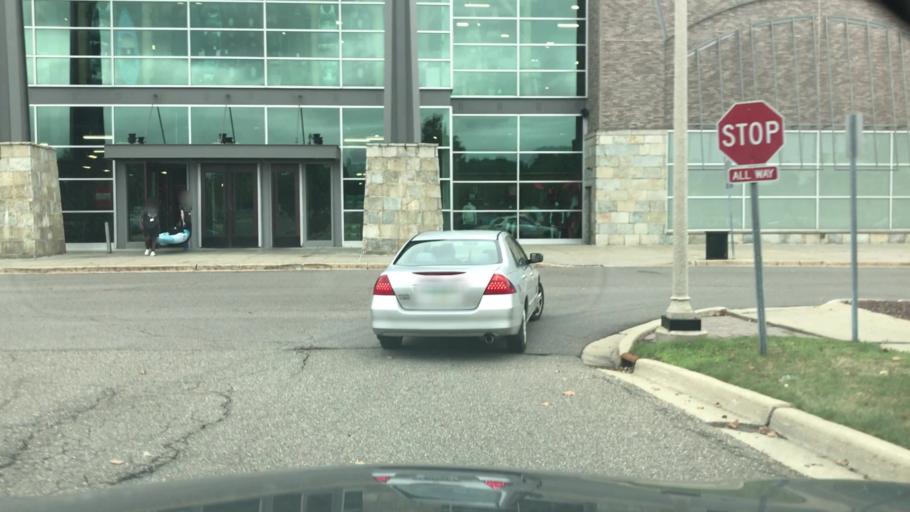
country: US
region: Michigan
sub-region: Oakland County
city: Novi
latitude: 42.4944
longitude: -83.4848
